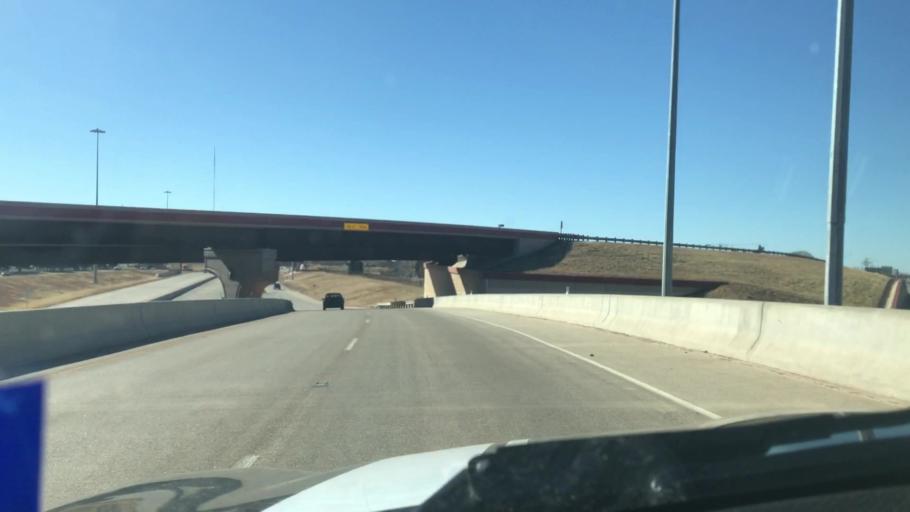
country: US
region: Texas
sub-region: Lubbock County
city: Lubbock
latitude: 33.5923
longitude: -101.8775
